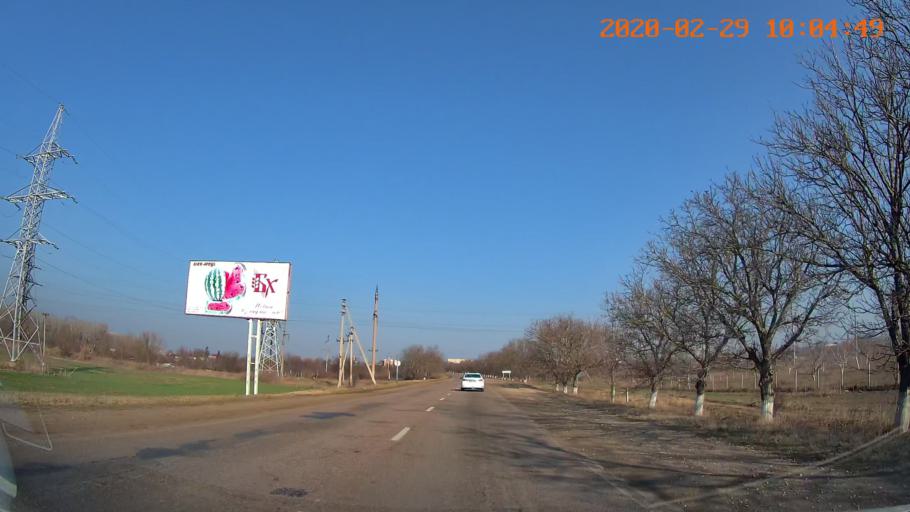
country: MD
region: Causeni
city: Chitcani
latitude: 46.8015
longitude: 29.6741
